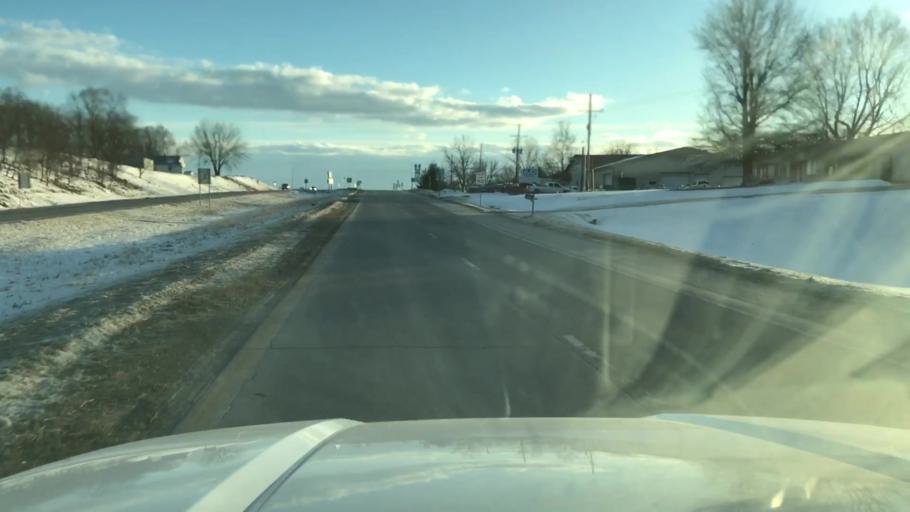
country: US
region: Missouri
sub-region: Andrew County
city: Country Club Village
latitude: 39.8627
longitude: -94.8093
